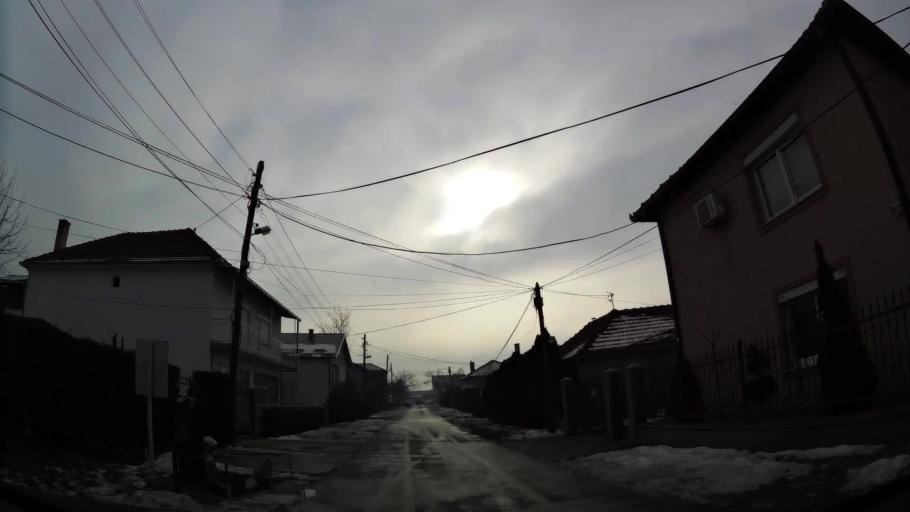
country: MK
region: Ilinden
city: Ilinden
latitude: 41.9928
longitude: 21.5844
